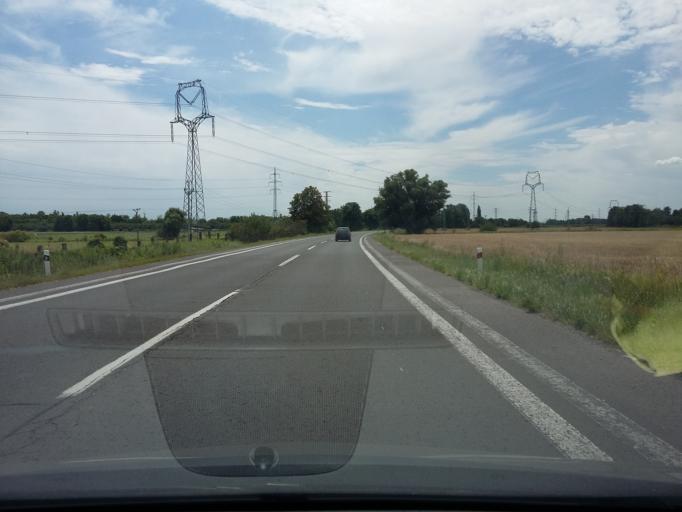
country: SK
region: Bratislavsky
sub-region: Okres Malacky
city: Malacky
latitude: 48.4851
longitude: 17.0125
